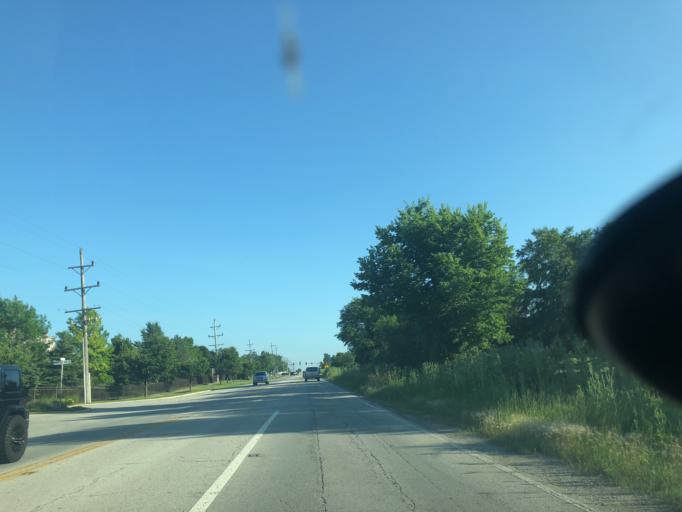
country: US
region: Illinois
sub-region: Will County
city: Mokena
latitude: 41.5604
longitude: -87.8904
